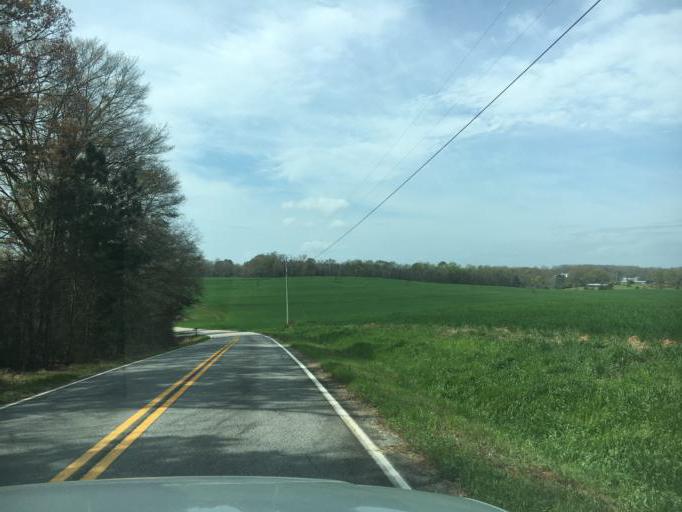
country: US
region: Georgia
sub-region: Franklin County
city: Lavonia
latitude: 34.4250
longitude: -83.0523
